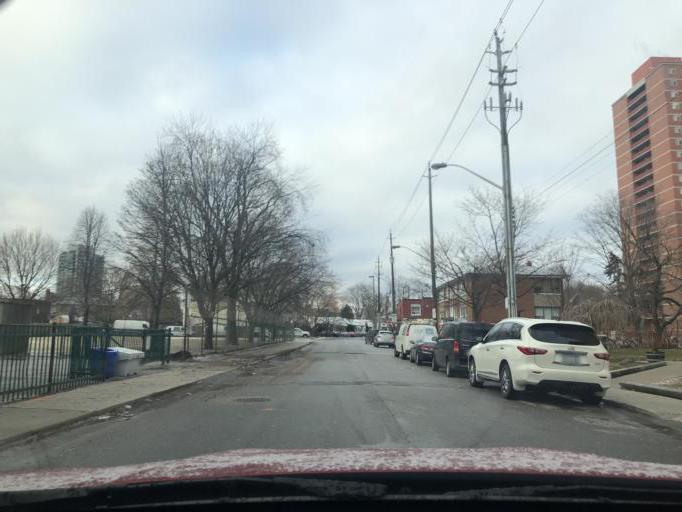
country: CA
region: Ontario
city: Toronto
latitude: 43.6878
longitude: -79.3518
